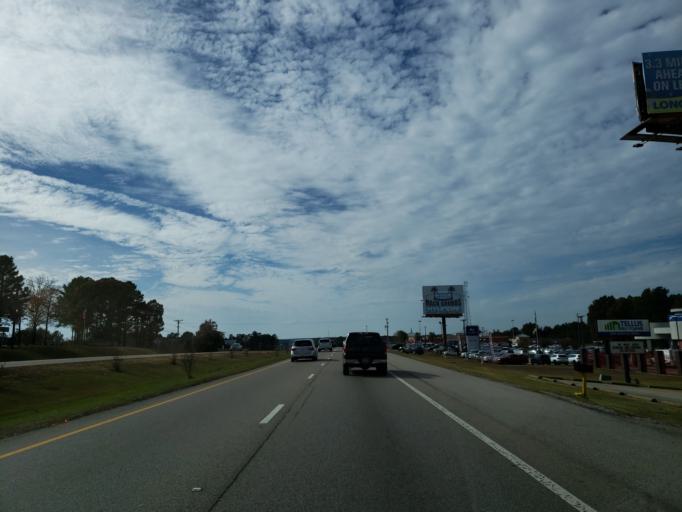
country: US
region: Mississippi
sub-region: Lamar County
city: West Hattiesburg
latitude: 31.3176
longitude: -89.4154
